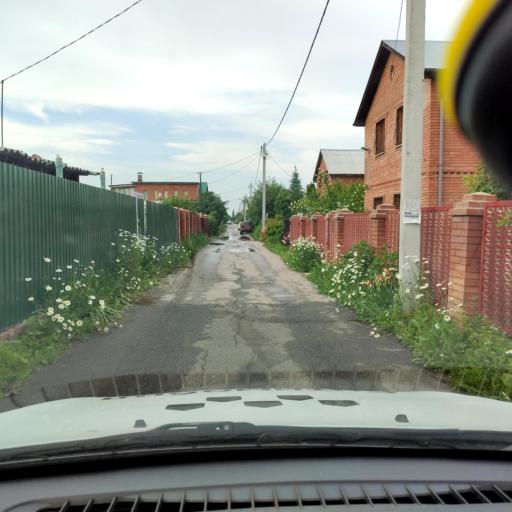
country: RU
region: Samara
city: Podstepki
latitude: 53.5805
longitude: 49.0801
